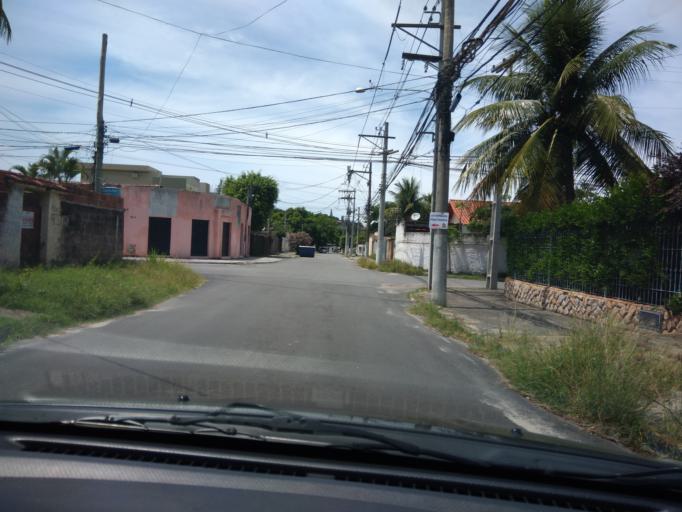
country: BR
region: Rio de Janeiro
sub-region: Niteroi
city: Niteroi
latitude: -22.9357
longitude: -43.0675
